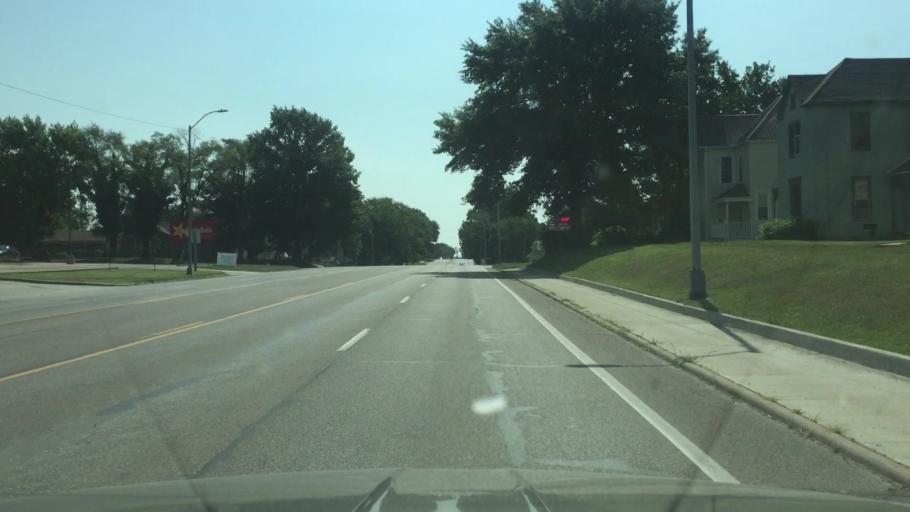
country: US
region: Missouri
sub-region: Pettis County
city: Sedalia
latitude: 38.7038
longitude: -93.2190
